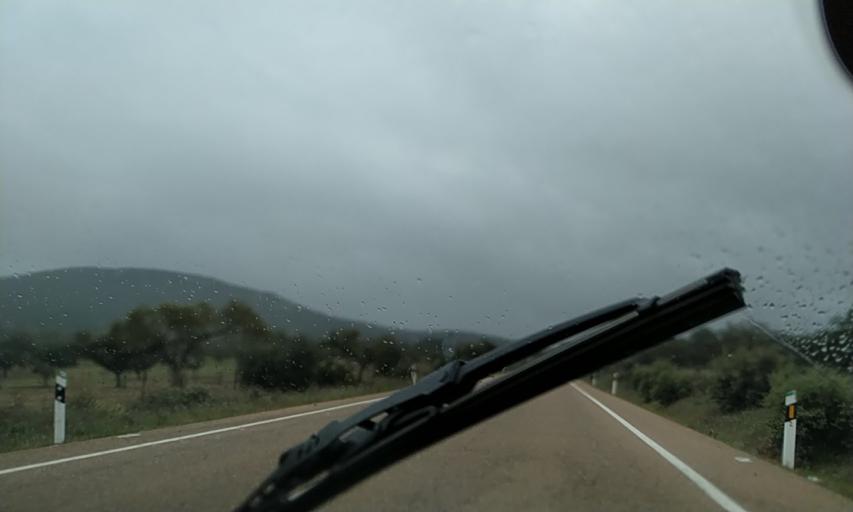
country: ES
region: Extremadura
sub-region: Provincia de Badajoz
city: Puebla de Obando
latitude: 39.2079
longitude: -6.5859
